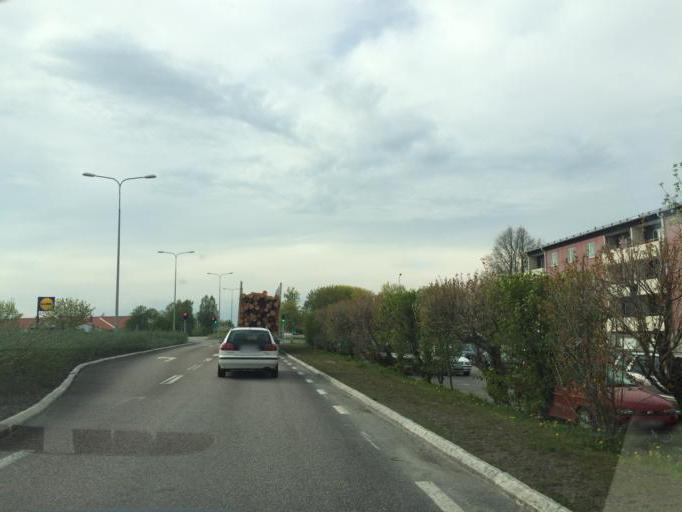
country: SE
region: Vaestmanland
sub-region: Kopings Kommun
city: Koping
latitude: 59.5127
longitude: 15.9836
